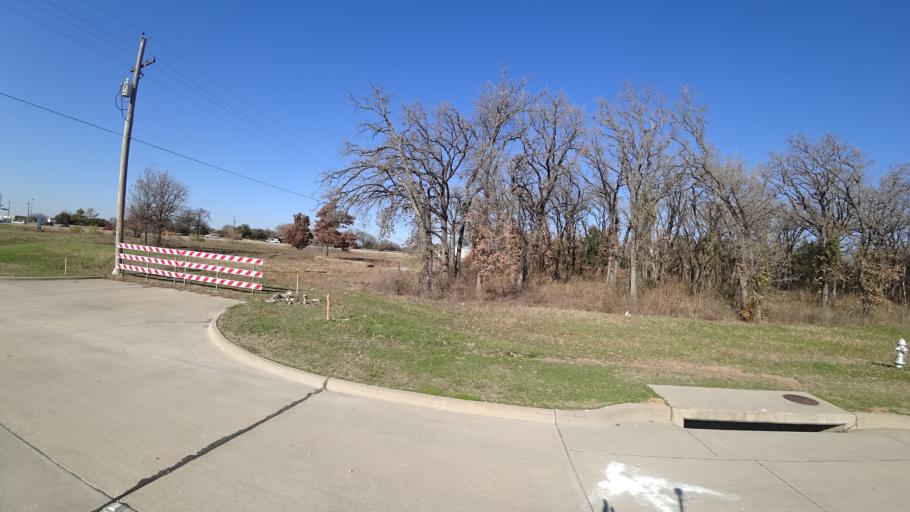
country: US
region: Texas
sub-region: Dallas County
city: Coppell
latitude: 32.9943
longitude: -97.0019
